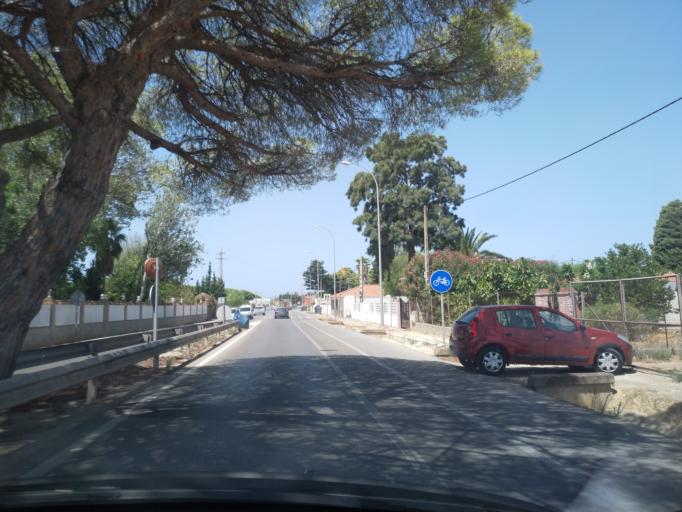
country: ES
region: Andalusia
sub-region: Provincia de Cadiz
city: Chiclana de la Frontera
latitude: 36.3942
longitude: -6.1544
